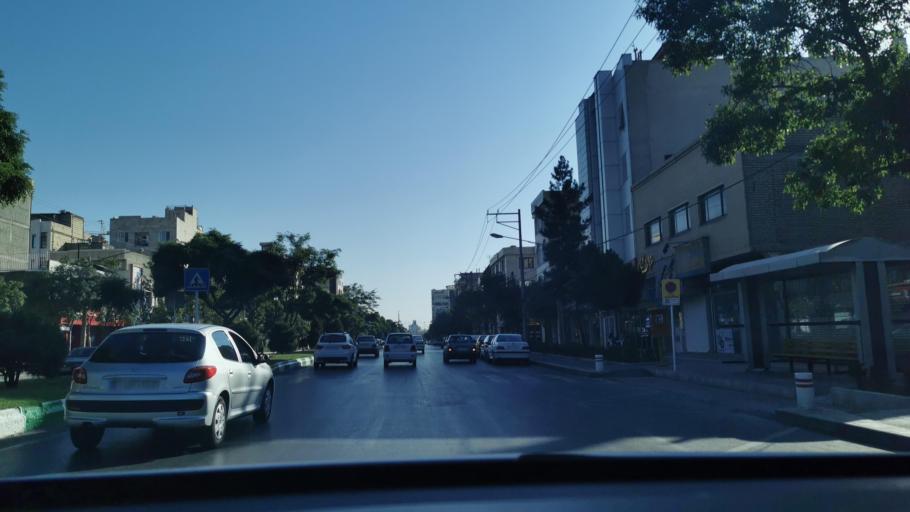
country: IR
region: Razavi Khorasan
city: Mashhad
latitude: 36.3168
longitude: 59.5100
